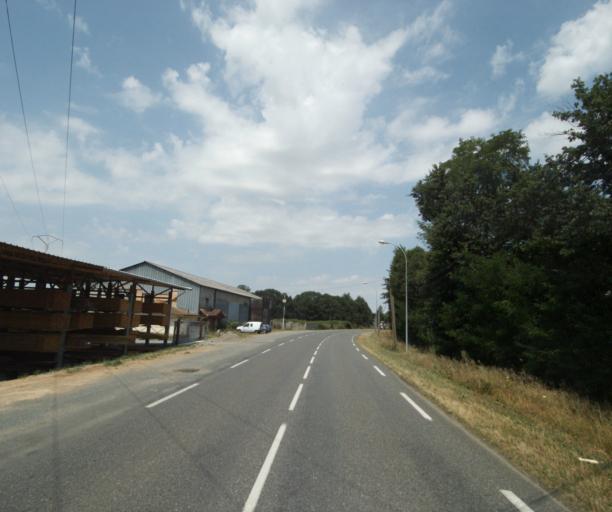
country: FR
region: Bourgogne
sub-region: Departement de Saone-et-Loire
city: Gueugnon
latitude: 46.5912
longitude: 4.0578
